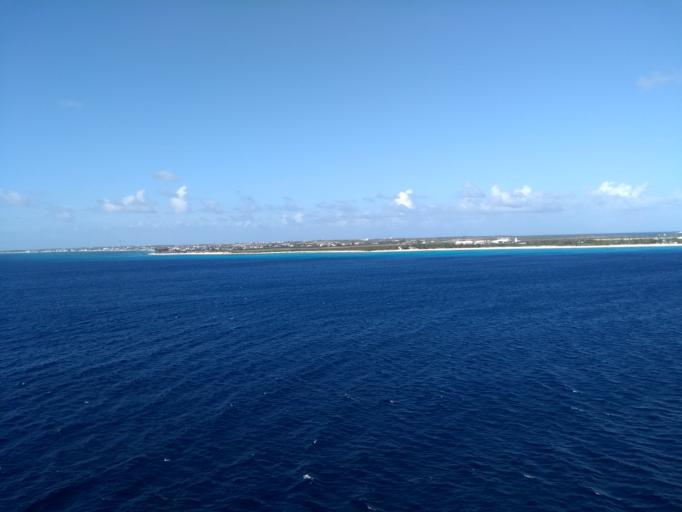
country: TC
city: Cockburn Town
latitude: 21.4354
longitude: -71.1608
